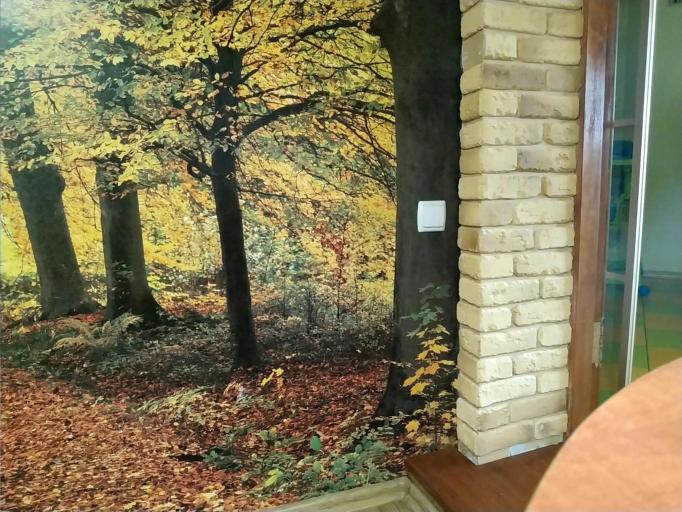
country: RU
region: Smolensk
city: Dorogobuzh
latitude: 54.9260
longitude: 33.3221
